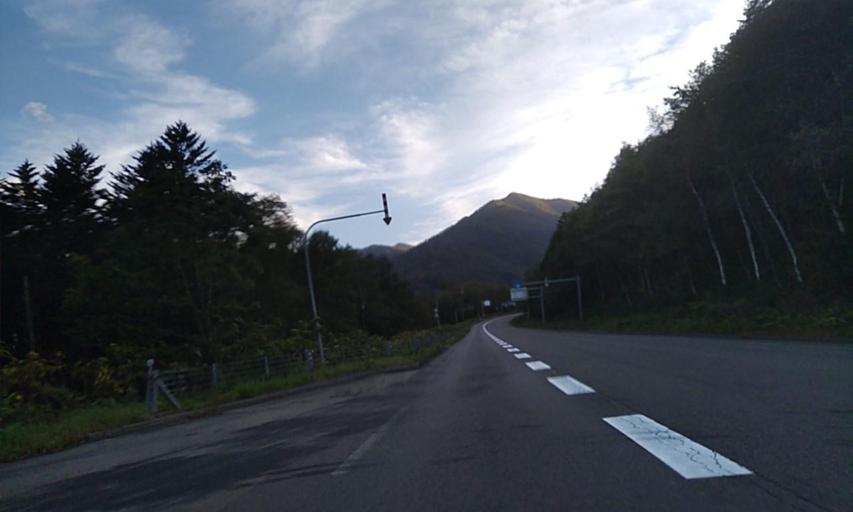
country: JP
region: Hokkaido
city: Otofuke
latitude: 42.9656
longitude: 142.8005
